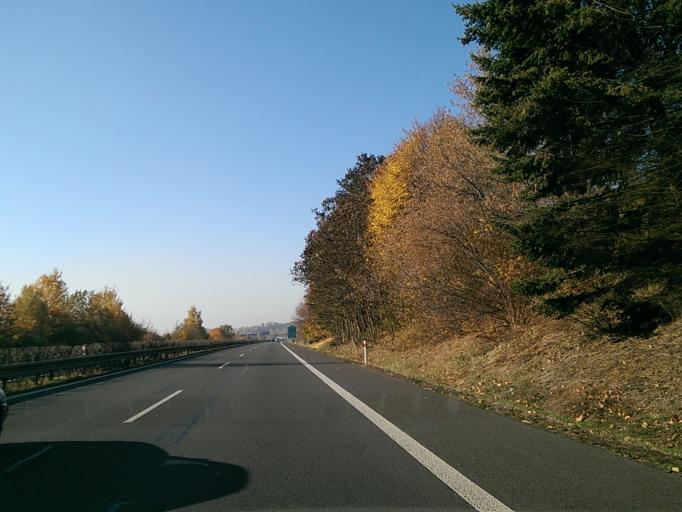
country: CZ
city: Prisovice
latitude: 50.5835
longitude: 15.0871
